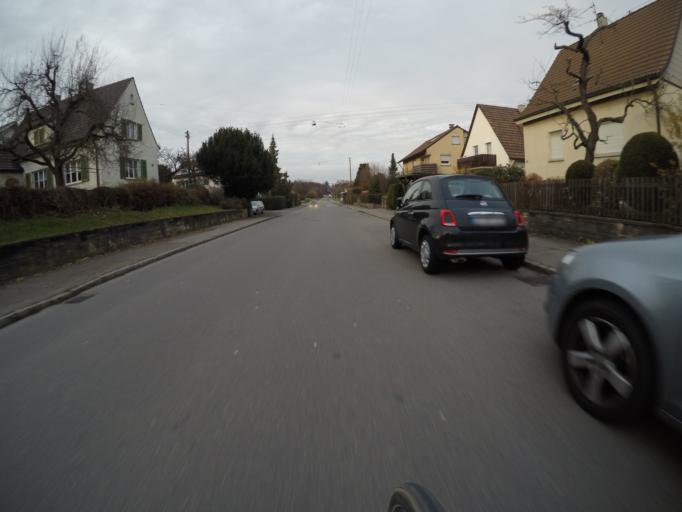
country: DE
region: Baden-Wuerttemberg
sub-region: Regierungsbezirk Stuttgart
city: Ostfildern
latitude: 48.7357
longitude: 9.2541
